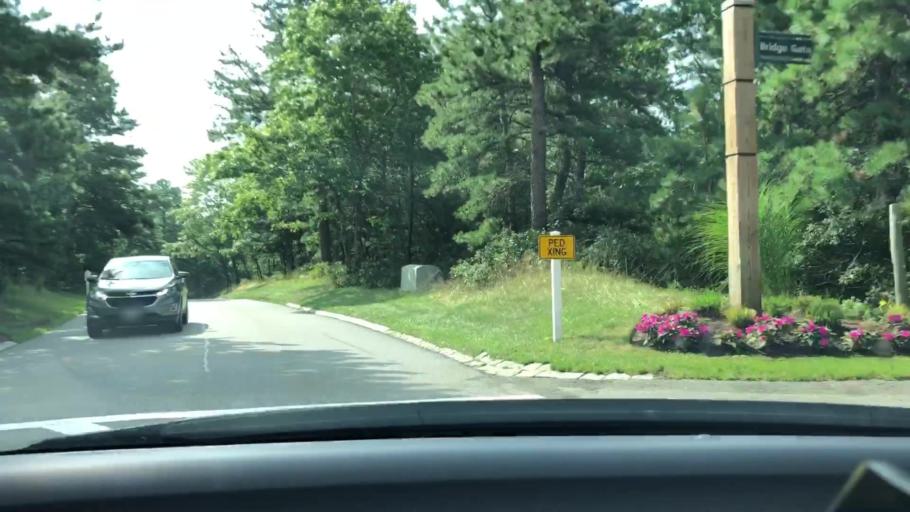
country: US
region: Massachusetts
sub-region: Plymouth County
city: White Island Shores
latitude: 41.8860
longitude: -70.6031
